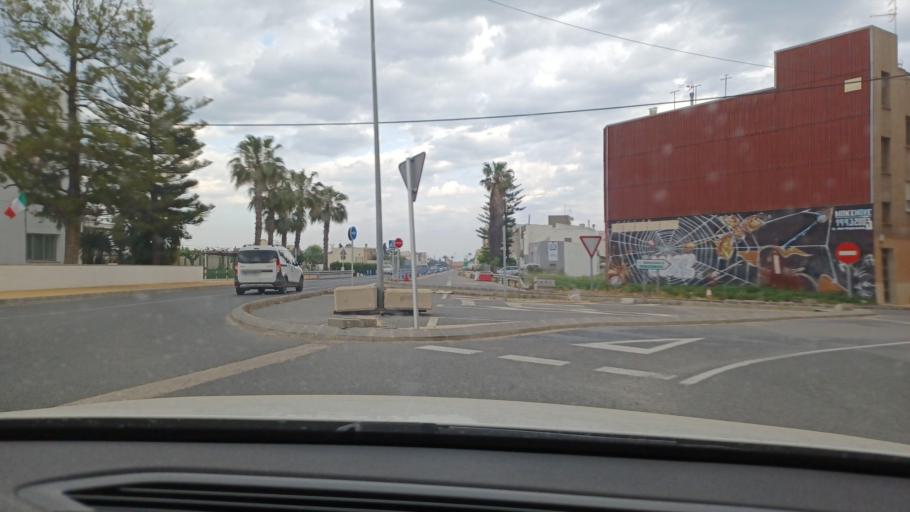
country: ES
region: Valencia
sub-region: Provincia de Castello
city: Benicarlo
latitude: 40.4242
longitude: 0.4229
